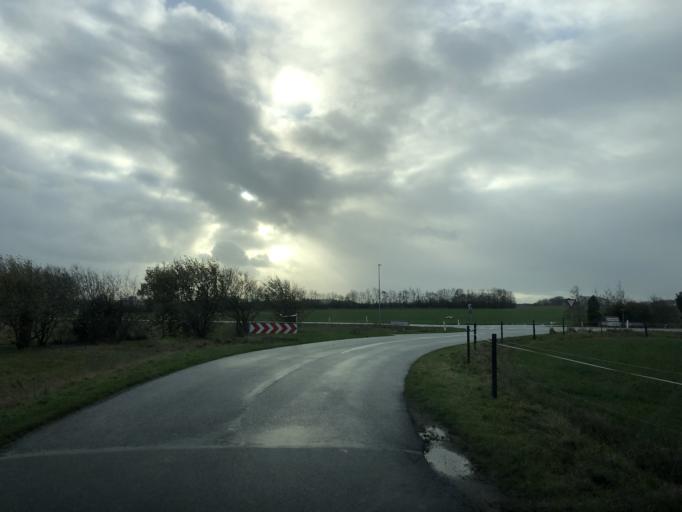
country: DK
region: North Denmark
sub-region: Rebild Kommune
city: Stovring
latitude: 56.8958
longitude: 9.7809
